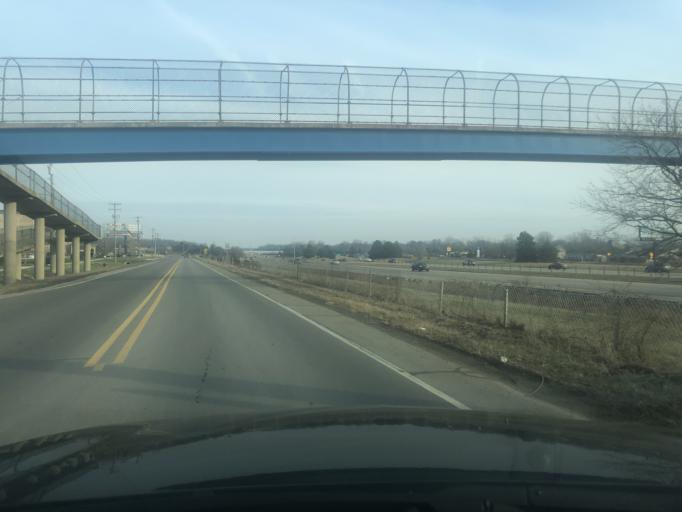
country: US
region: Michigan
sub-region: Wayne County
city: Belleville
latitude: 42.2201
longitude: -83.4942
